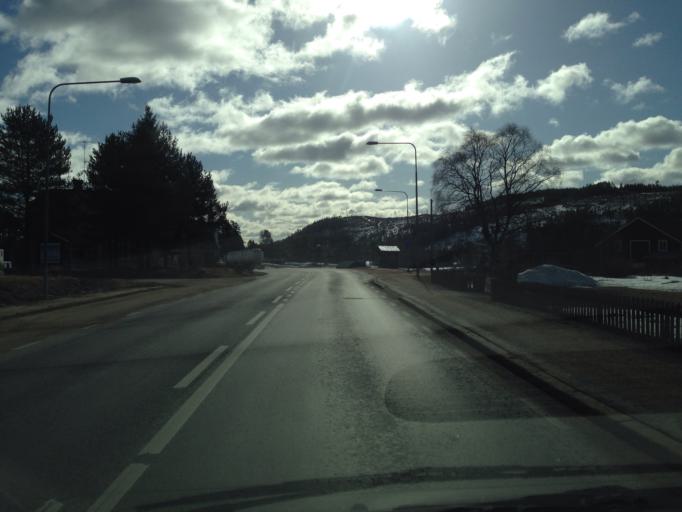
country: SE
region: Gaevleborg
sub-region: Ljusdals Kommun
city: Farila
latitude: 61.9846
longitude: 15.3072
